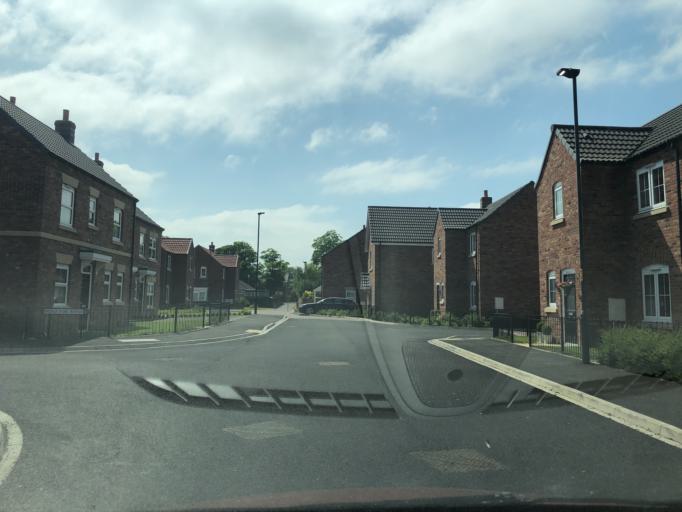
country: GB
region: England
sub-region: North Yorkshire
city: Bedale
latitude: 54.3047
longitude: -1.5575
